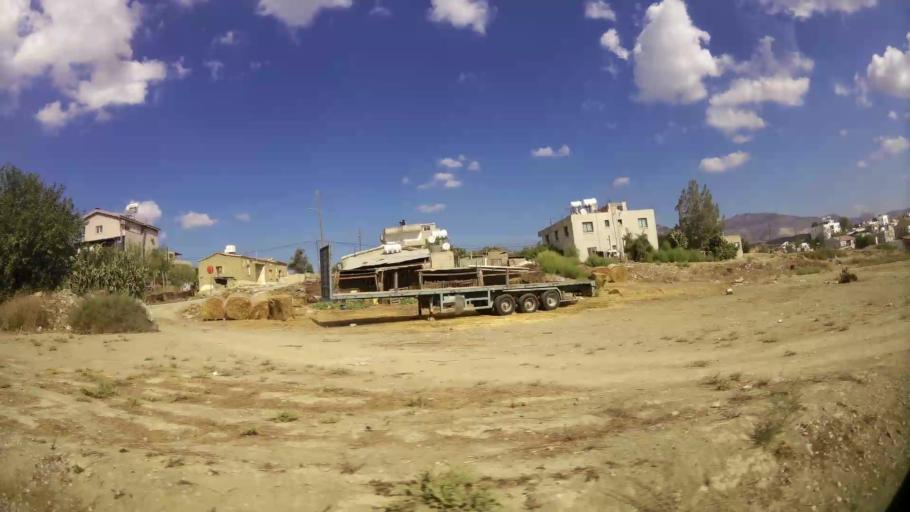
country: CY
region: Lefkosia
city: Nicosia
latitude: 35.2224
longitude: 33.3816
